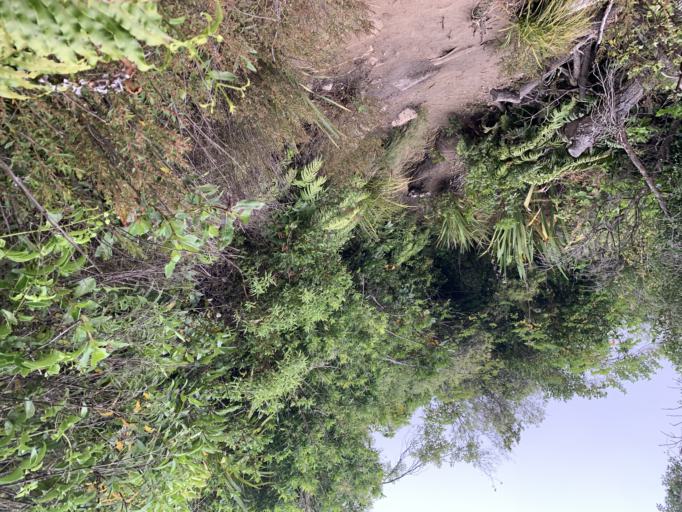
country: NZ
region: Waikato
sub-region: Taupo District
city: Taupo
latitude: -38.6976
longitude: 176.1516
